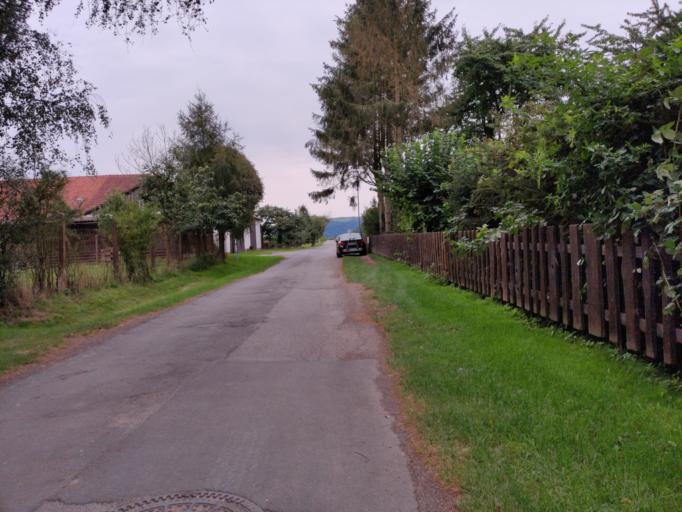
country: DE
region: Lower Saxony
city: Bodenwerder
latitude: 51.9585
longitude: 9.5052
